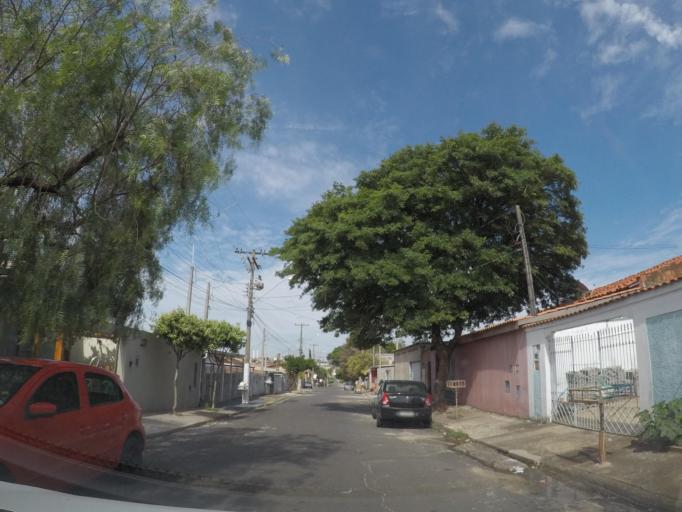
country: BR
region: Sao Paulo
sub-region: Hortolandia
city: Hortolandia
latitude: -22.8375
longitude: -47.1834
